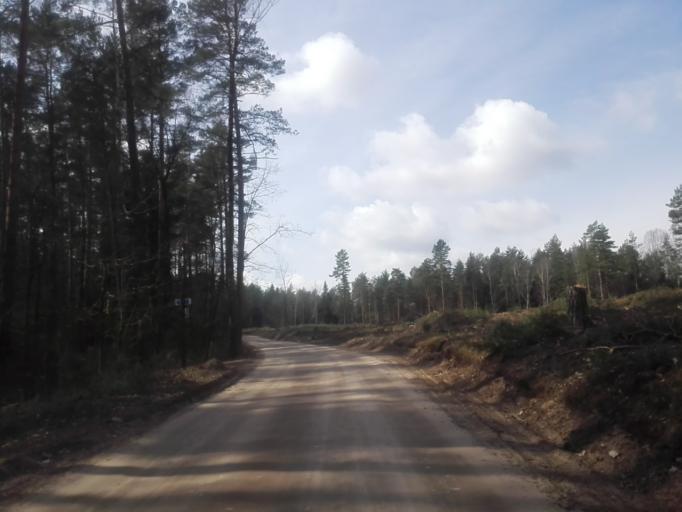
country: PL
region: Podlasie
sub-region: Powiat sejnenski
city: Sejny
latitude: 54.0259
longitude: 23.4108
